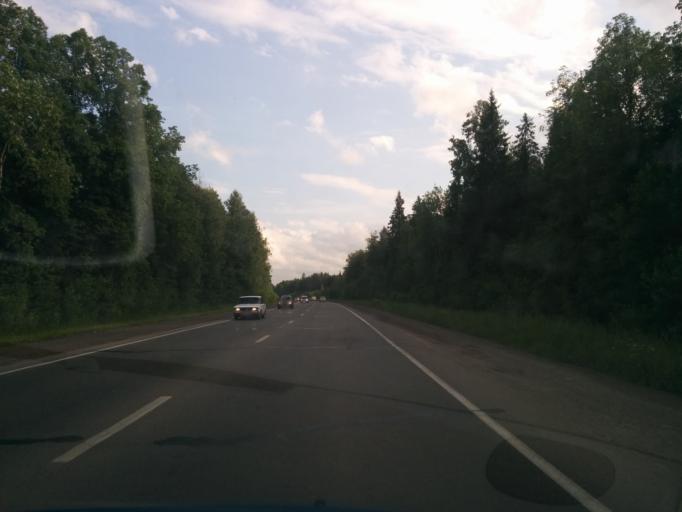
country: RU
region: Perm
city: Polazna
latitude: 58.1031
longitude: 56.4251
